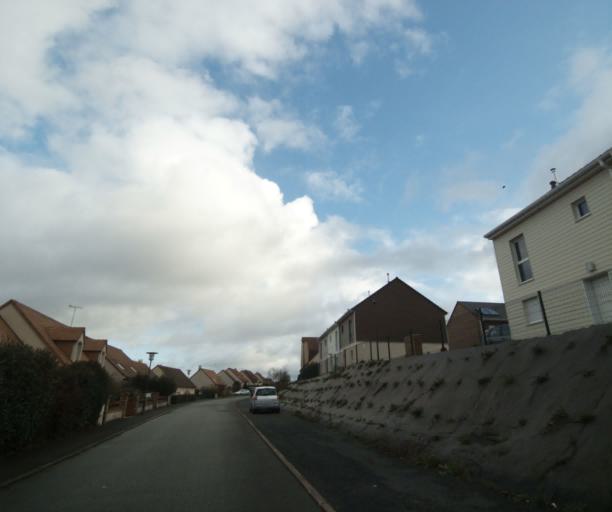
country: FR
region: Pays de la Loire
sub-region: Departement de la Sarthe
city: La Chapelle-Saint-Aubin
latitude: 48.0111
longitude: 0.1632
